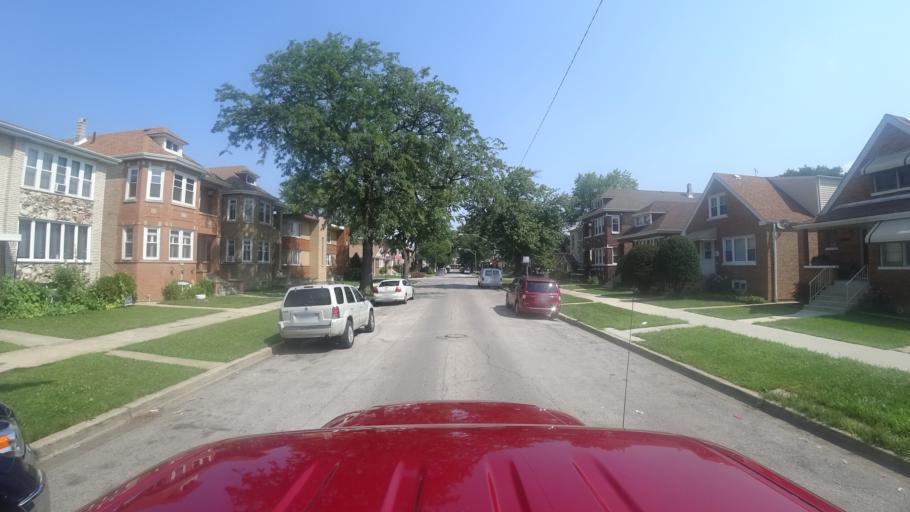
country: US
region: Illinois
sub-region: Cook County
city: Cicero
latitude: 41.8054
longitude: -87.7322
